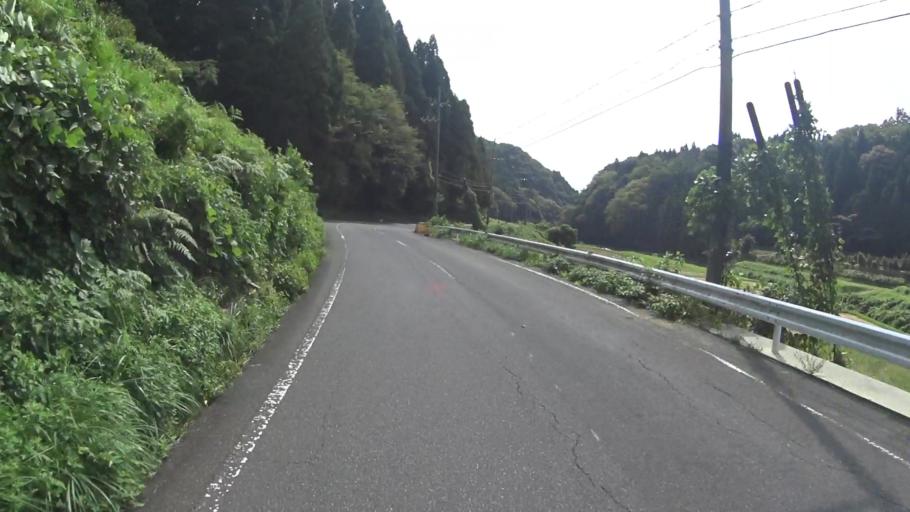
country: JP
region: Kyoto
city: Miyazu
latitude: 35.6678
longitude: 135.2498
